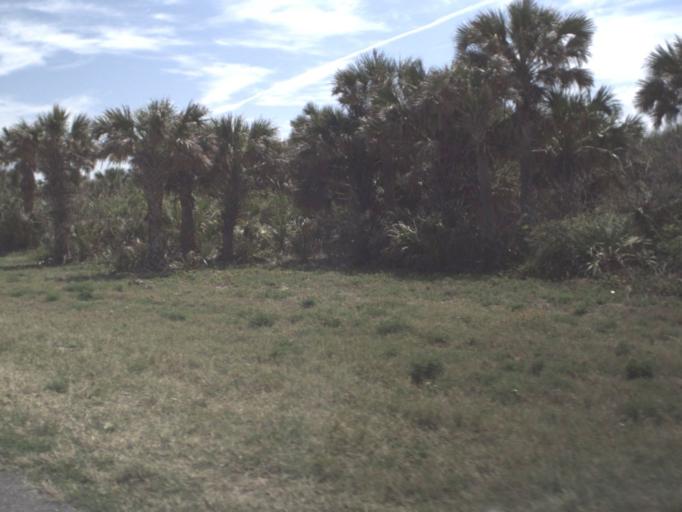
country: US
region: Florida
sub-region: Flagler County
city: Palm Coast
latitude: 29.5508
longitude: -81.1624
